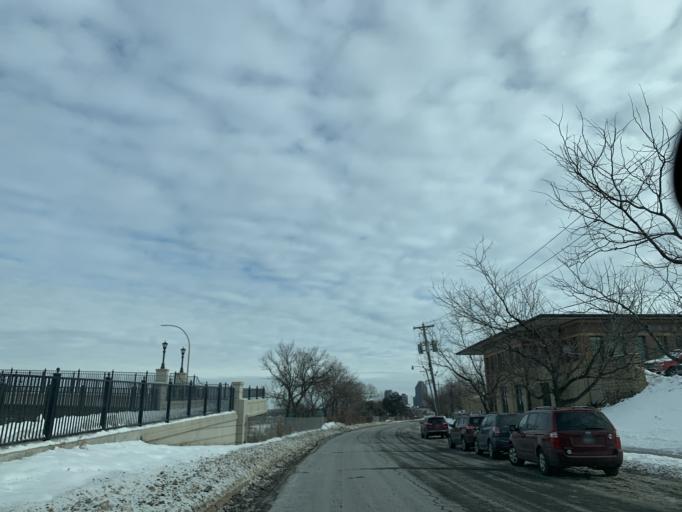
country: US
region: Minnesota
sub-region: Ramsey County
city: Saint Paul
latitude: 44.9514
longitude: -93.1210
